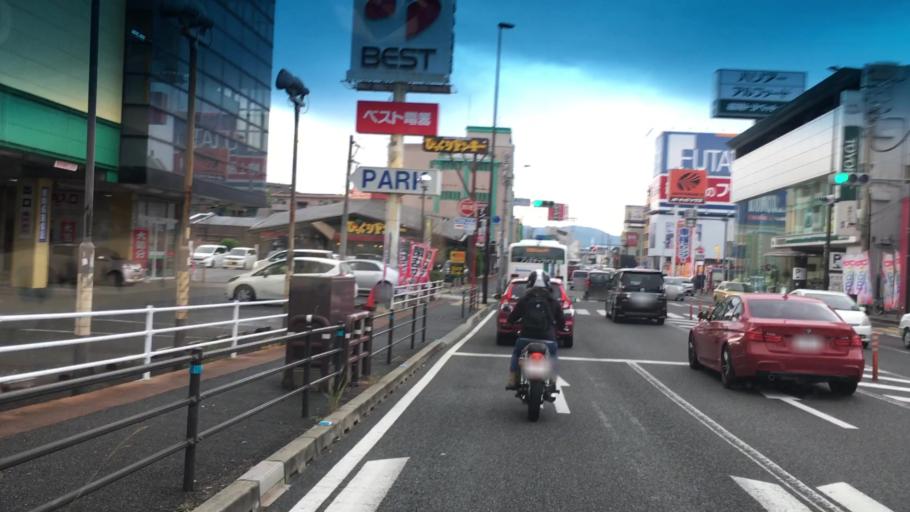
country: JP
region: Fukuoka
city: Fukuoka-shi
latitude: 33.5673
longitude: 130.3456
